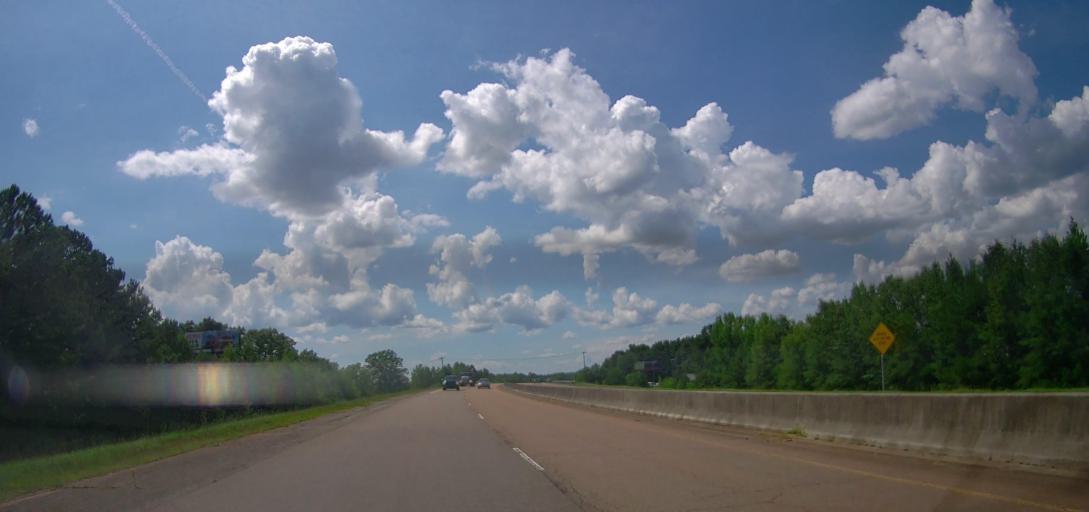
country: US
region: Mississippi
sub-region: Lowndes County
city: New Hope
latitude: 33.5095
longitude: -88.3616
